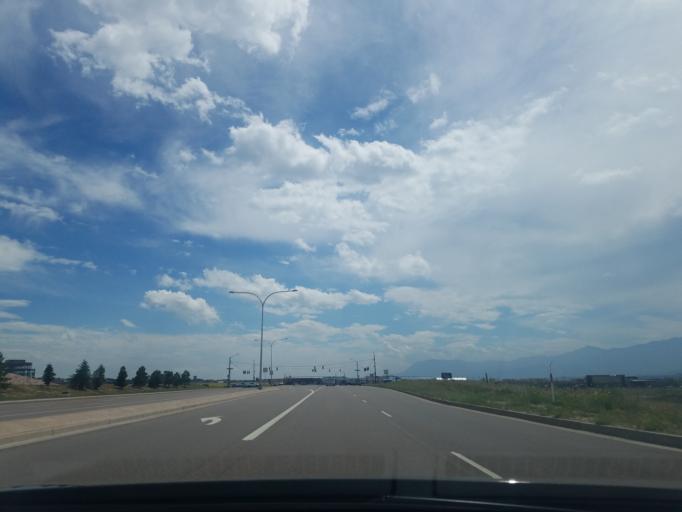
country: US
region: Colorado
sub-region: El Paso County
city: Gleneagle
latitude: 38.9926
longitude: -104.7981
